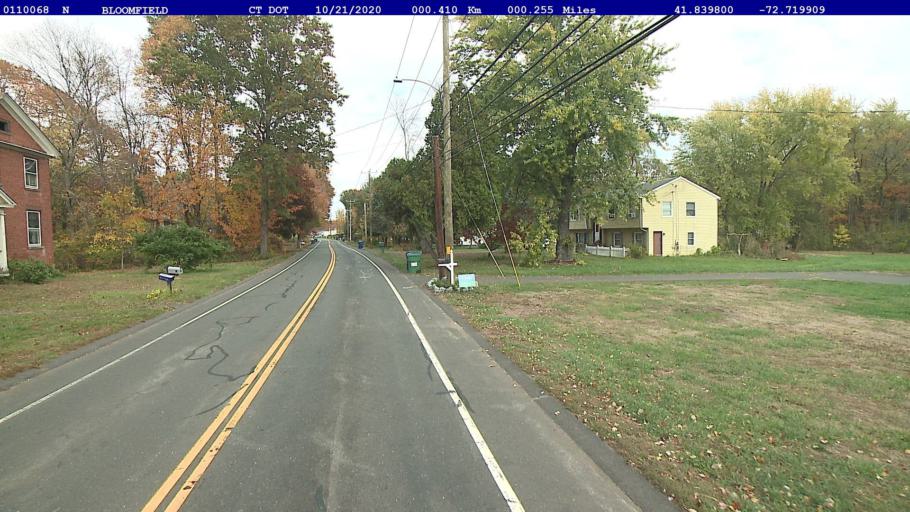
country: US
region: Connecticut
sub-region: Hartford County
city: Blue Hills
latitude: 41.8398
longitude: -72.7199
